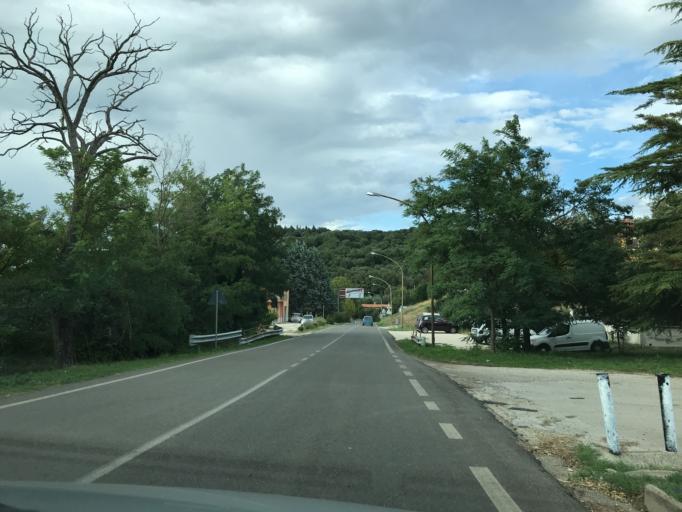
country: IT
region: Umbria
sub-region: Provincia di Terni
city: Guardea
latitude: 42.6281
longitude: 12.2964
